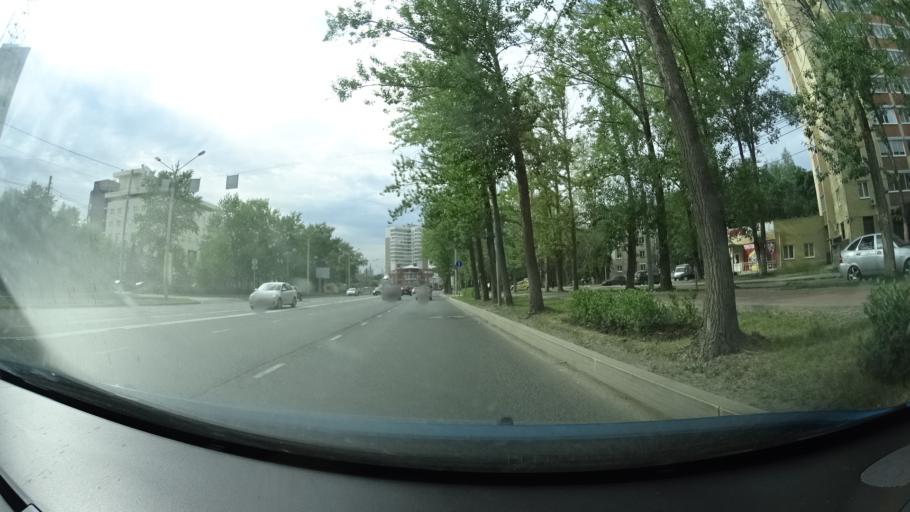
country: RU
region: Perm
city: Perm
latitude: 57.9933
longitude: 56.2906
